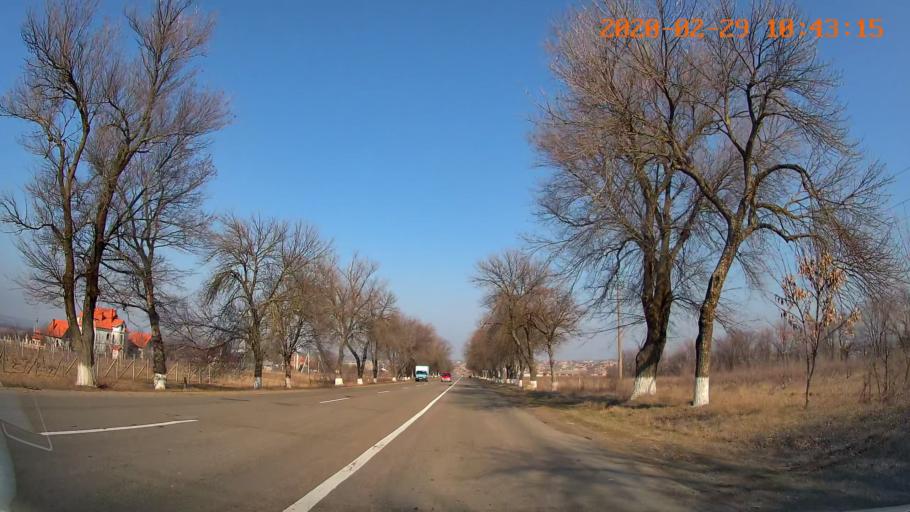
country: MD
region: Telenesti
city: Grigoriopol
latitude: 47.0591
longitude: 29.4044
